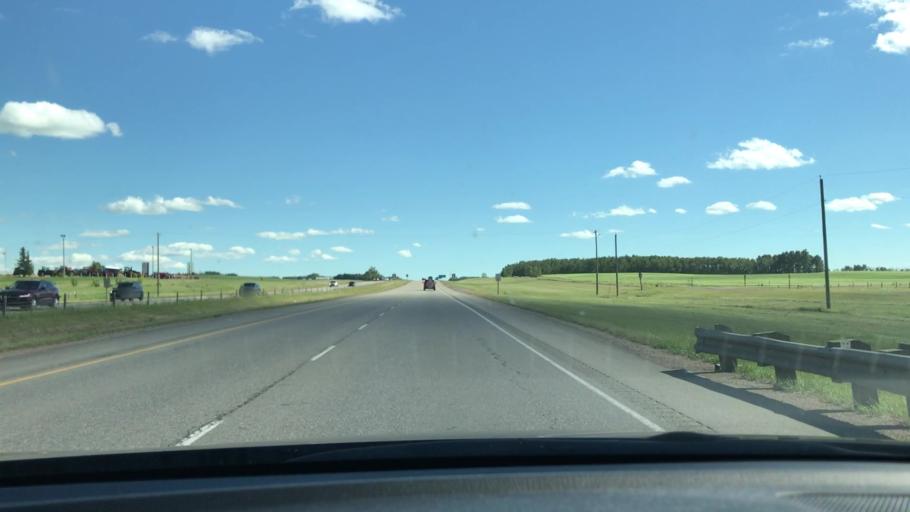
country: CA
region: Alberta
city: Penhold
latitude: 52.1735
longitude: -113.8141
